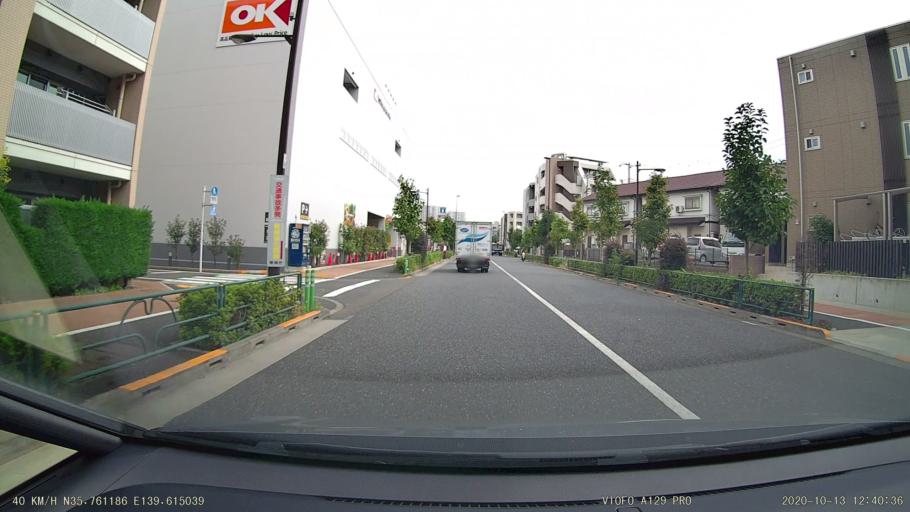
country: JP
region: Saitama
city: Wako
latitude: 35.7611
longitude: 139.6152
